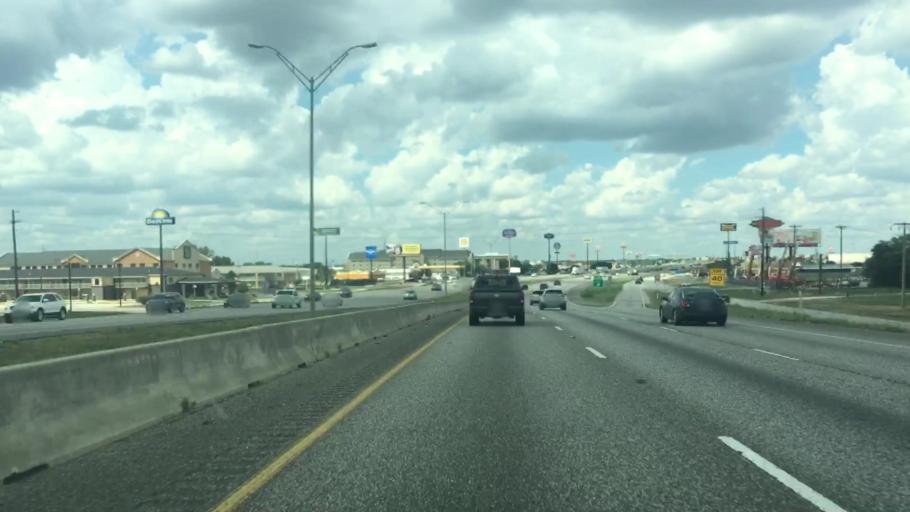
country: US
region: Texas
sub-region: McLennan County
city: Bellmead
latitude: 31.5964
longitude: -97.1090
